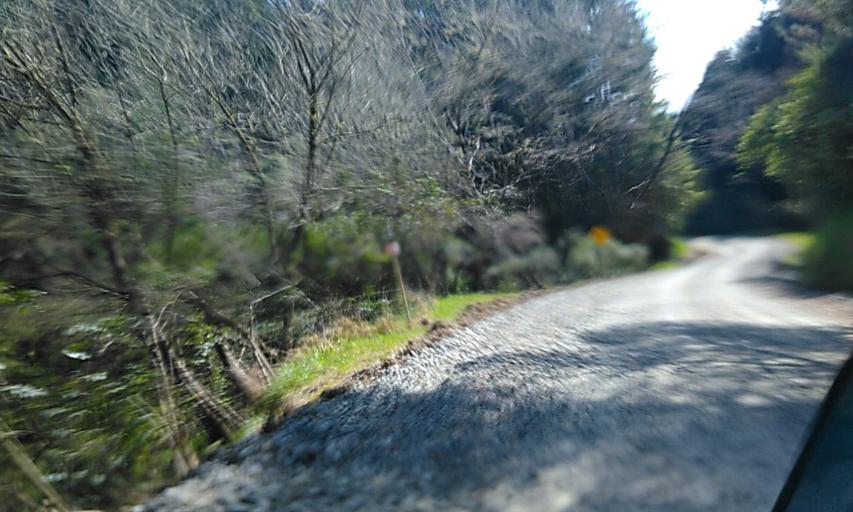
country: NZ
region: Gisborne
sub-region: Gisborne District
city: Gisborne
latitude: -38.2138
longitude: 178.0666
